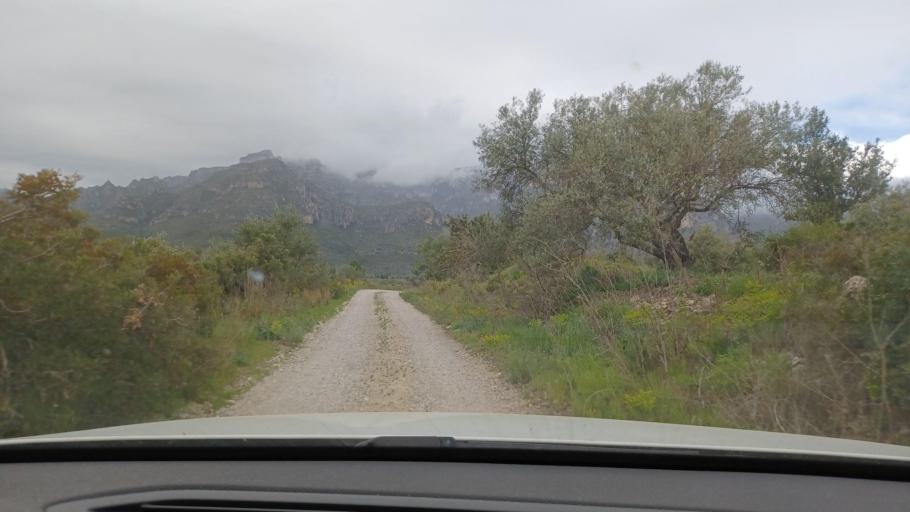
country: ES
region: Catalonia
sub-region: Provincia de Tarragona
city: Mas de Barberans
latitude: 40.8013
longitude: 0.4157
